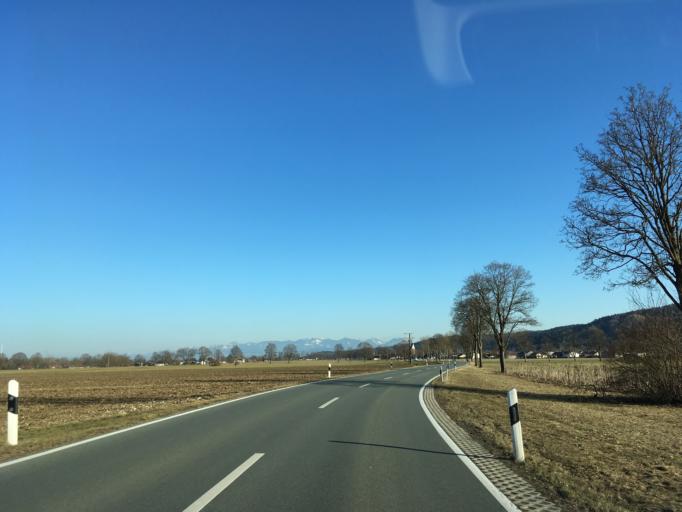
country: DE
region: Bavaria
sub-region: Upper Bavaria
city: Vagen
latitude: 47.8803
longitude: 11.8737
